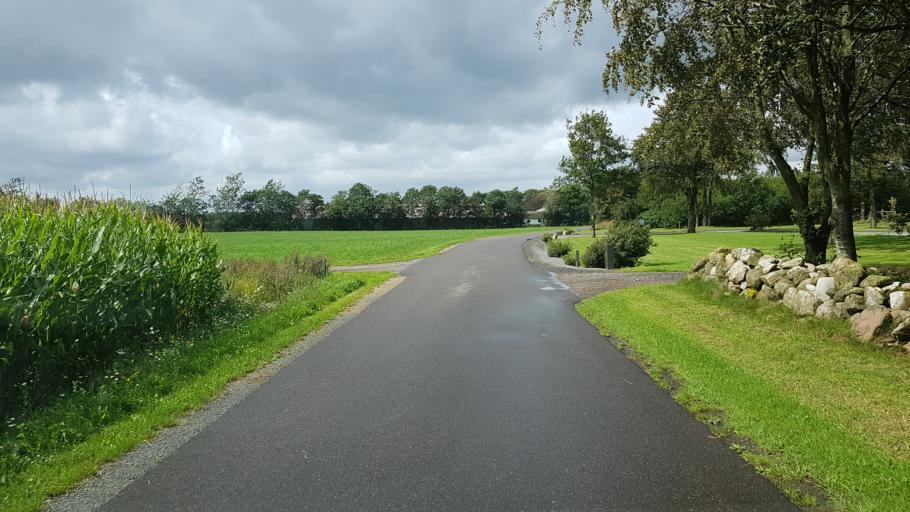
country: DK
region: South Denmark
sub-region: Vejen Kommune
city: Holsted
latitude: 55.6004
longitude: 8.8505
